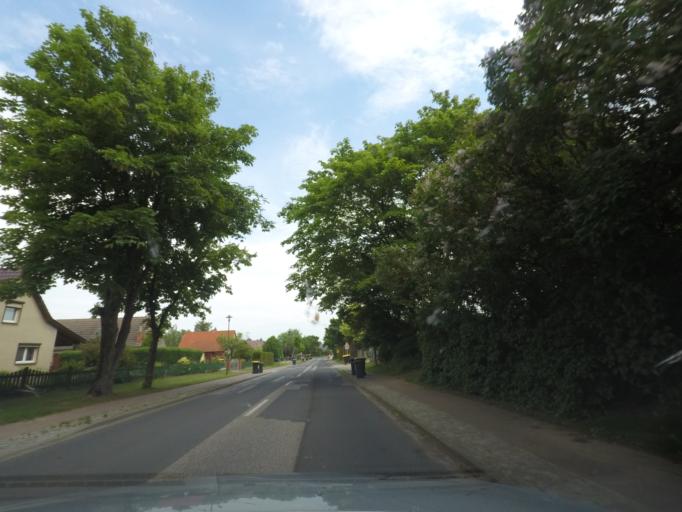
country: DE
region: Brandenburg
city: Schenkenberg
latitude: 53.3447
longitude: 13.9455
